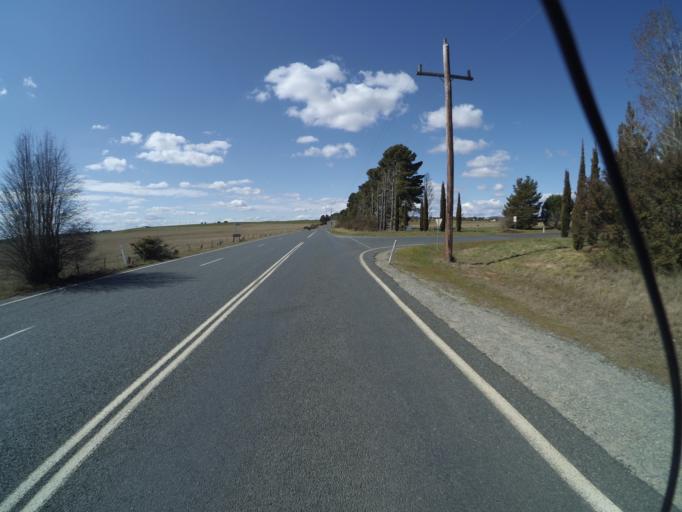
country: AU
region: New South Wales
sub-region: Palerang
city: Bungendore
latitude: -35.2252
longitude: 149.4547
